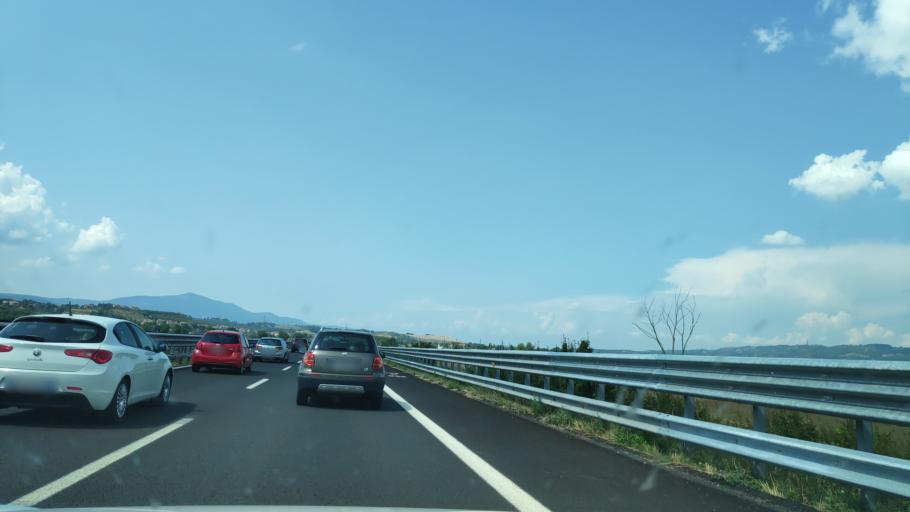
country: IT
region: Umbria
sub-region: Provincia di Terni
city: Fabro Scalo
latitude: 42.8625
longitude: 12.0357
